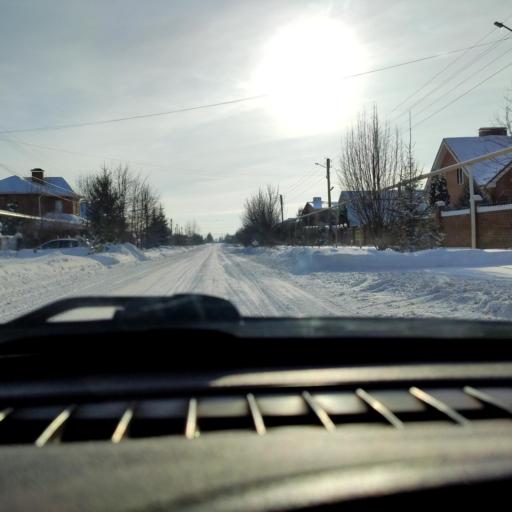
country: RU
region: Samara
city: Podstepki
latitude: 53.5175
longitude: 49.1811
